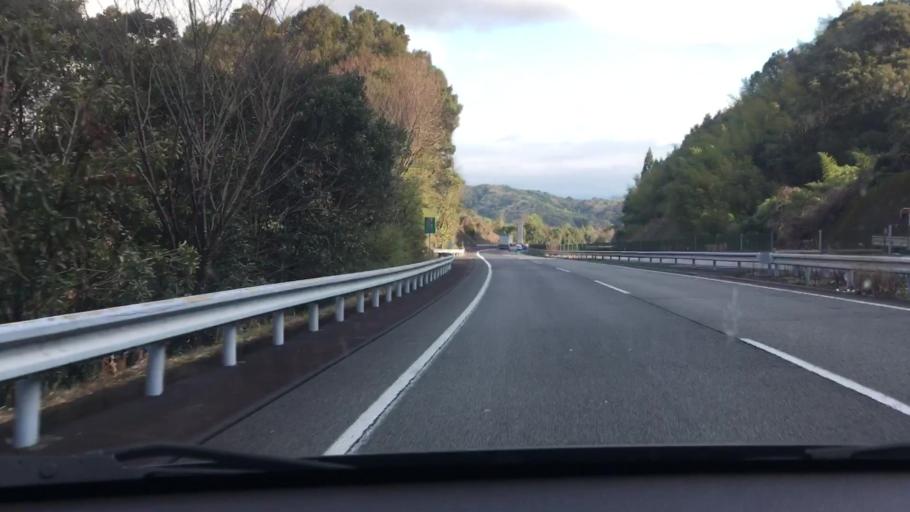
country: JP
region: Kumamoto
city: Hitoyoshi
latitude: 32.2672
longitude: 130.7630
